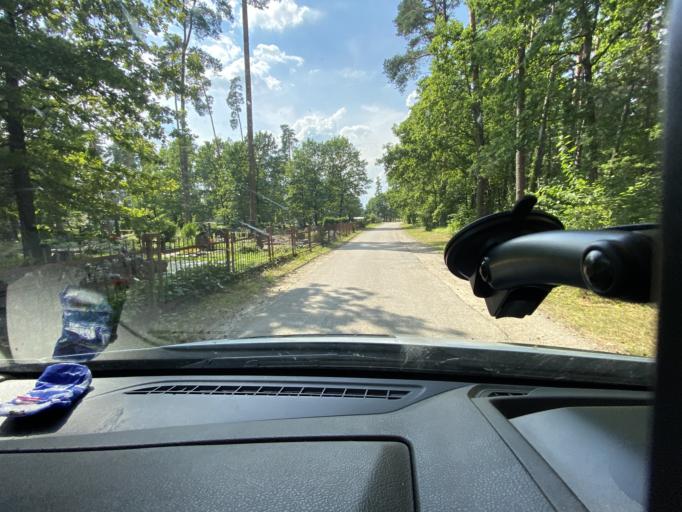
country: LT
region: Kauno apskritis
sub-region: Kauno rajonas
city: Karmelava
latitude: 54.9743
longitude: 24.0468
